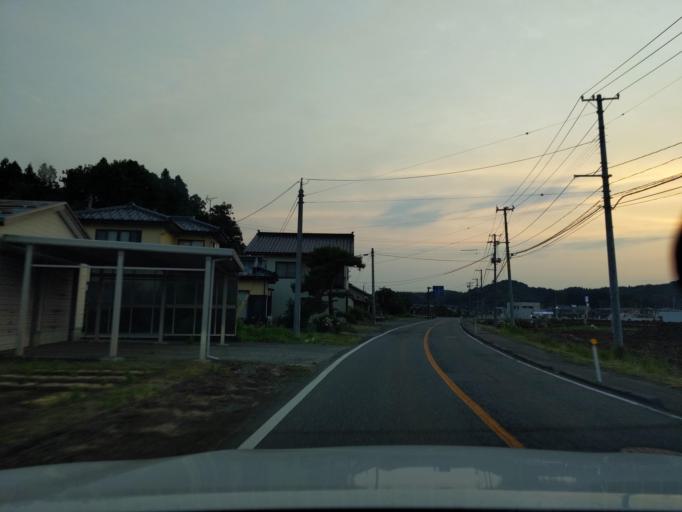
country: JP
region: Niigata
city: Kashiwazaki
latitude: 37.4462
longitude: 138.6442
